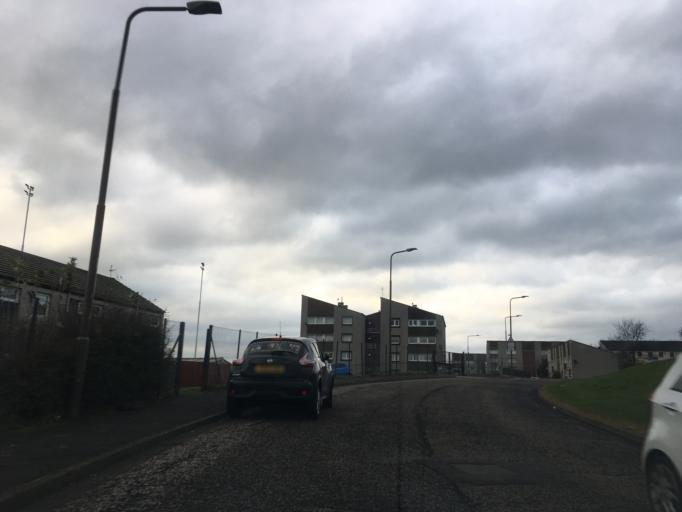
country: GB
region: Scotland
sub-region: Edinburgh
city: Currie
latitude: 55.9177
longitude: -3.2924
